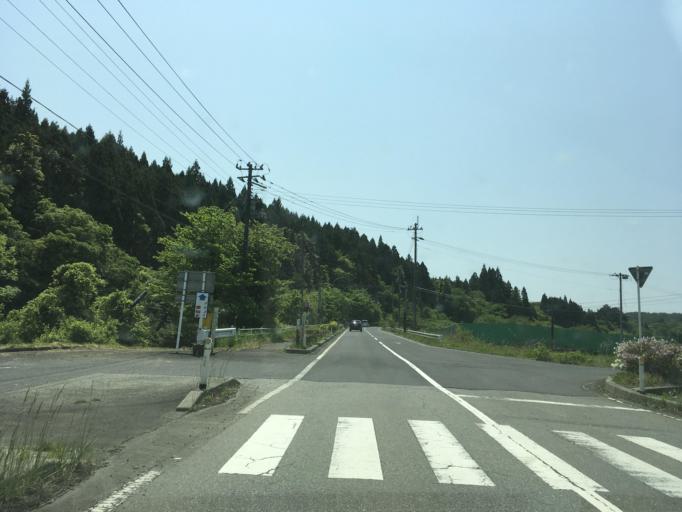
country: JP
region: Iwate
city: Ofunato
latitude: 38.8718
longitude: 141.5368
